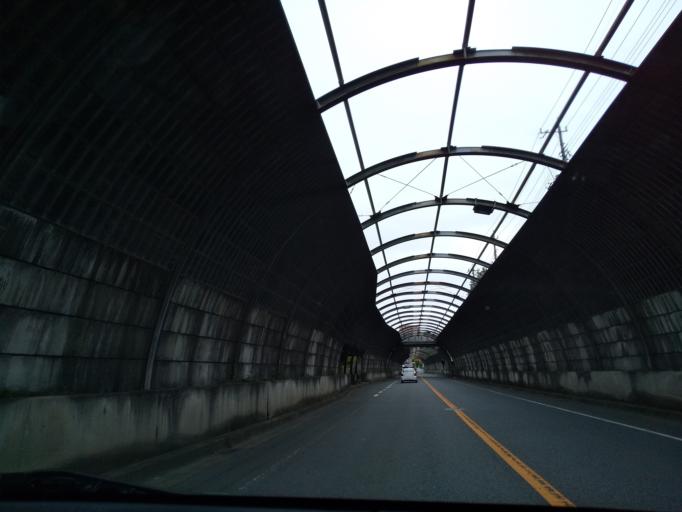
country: JP
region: Kanagawa
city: Zama
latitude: 35.5109
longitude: 139.4108
